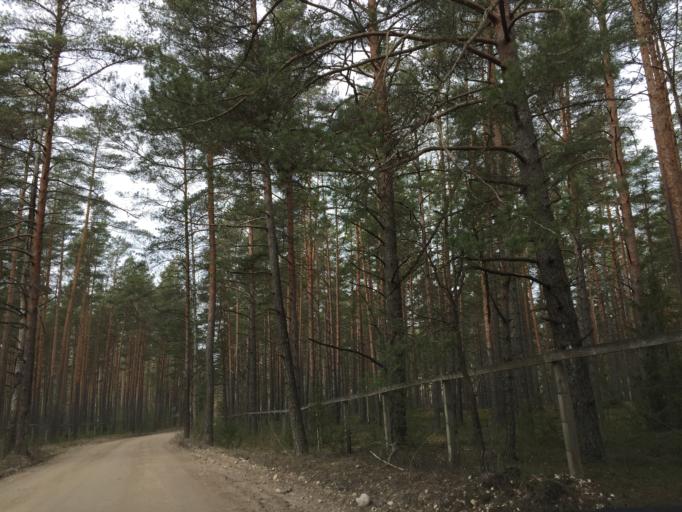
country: LV
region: Garkalne
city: Garkalne
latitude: 57.0706
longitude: 24.4586
